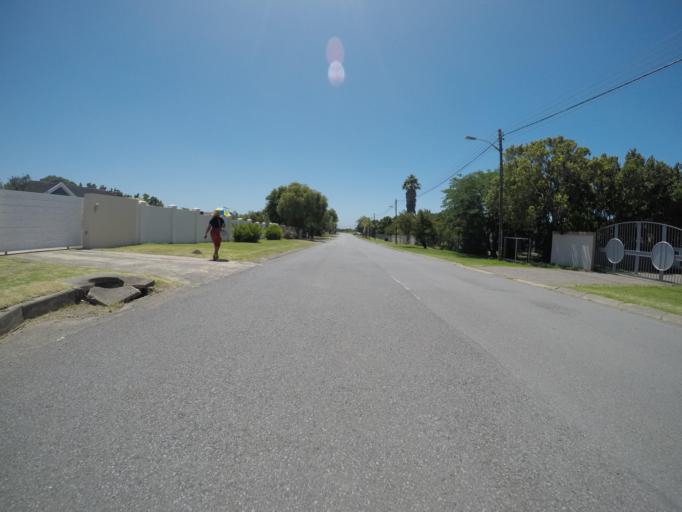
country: ZA
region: Eastern Cape
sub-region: Buffalo City Metropolitan Municipality
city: East London
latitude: -32.9662
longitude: 27.9482
